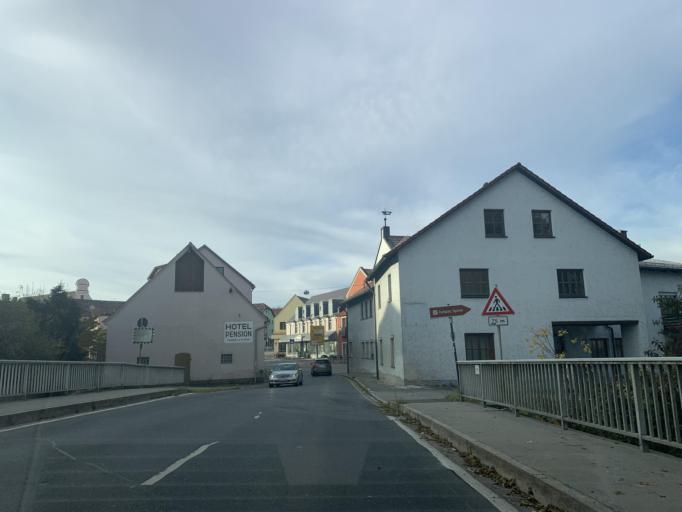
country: DE
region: Bavaria
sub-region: Upper Palatinate
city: Neunburg vorm Wald
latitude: 49.3498
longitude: 12.3823
